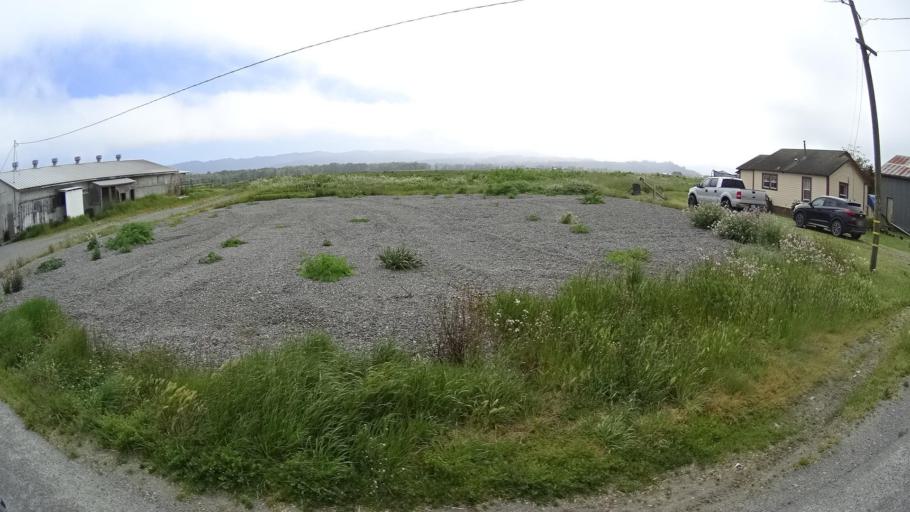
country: US
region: California
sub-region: Humboldt County
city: Fortuna
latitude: 40.5709
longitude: -124.1879
